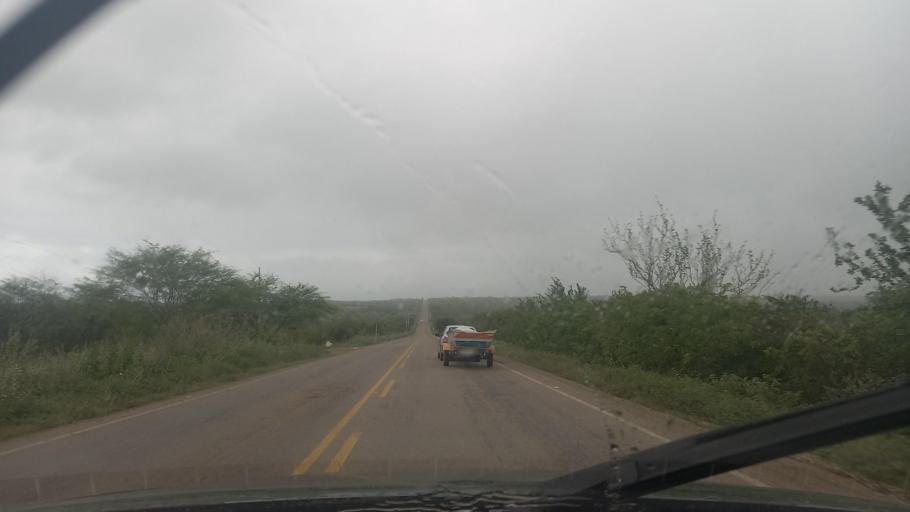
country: BR
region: Bahia
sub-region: Paulo Afonso
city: Paulo Afonso
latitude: -9.3423
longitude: -38.2821
